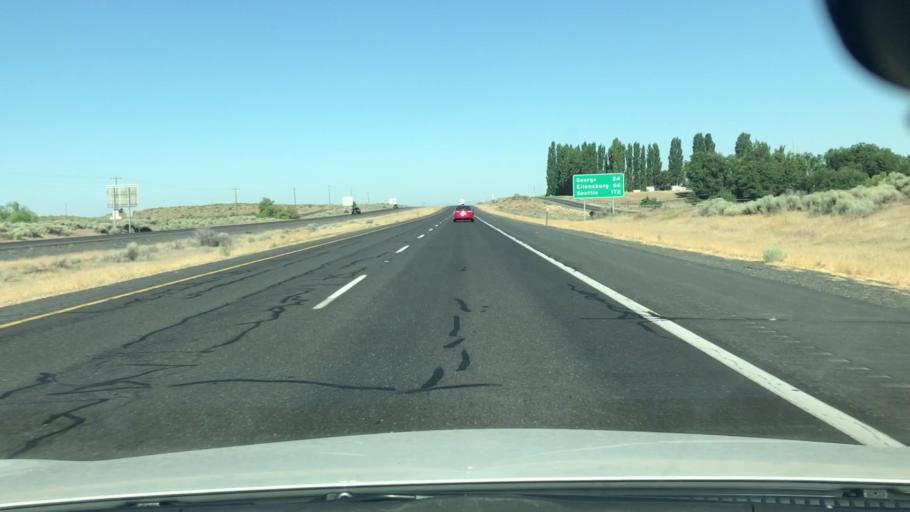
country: US
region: Washington
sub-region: Grant County
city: Cascade Valley
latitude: 47.1042
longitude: -119.3650
